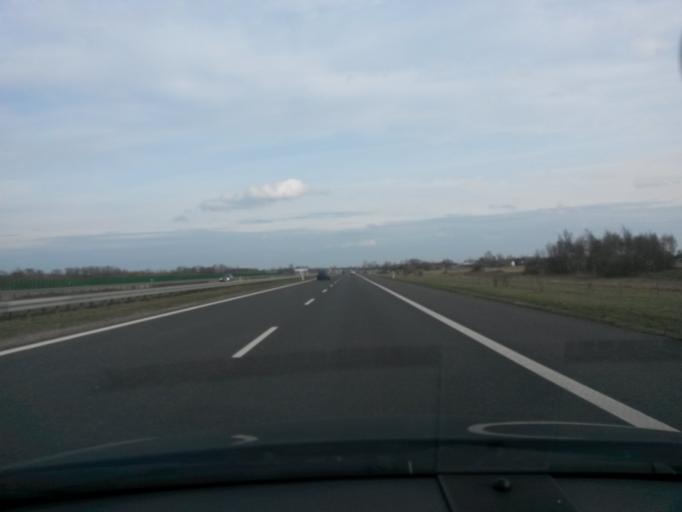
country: PL
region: Greater Poland Voivodeship
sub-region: Powiat kolski
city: Dabie
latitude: 52.0583
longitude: 18.8364
